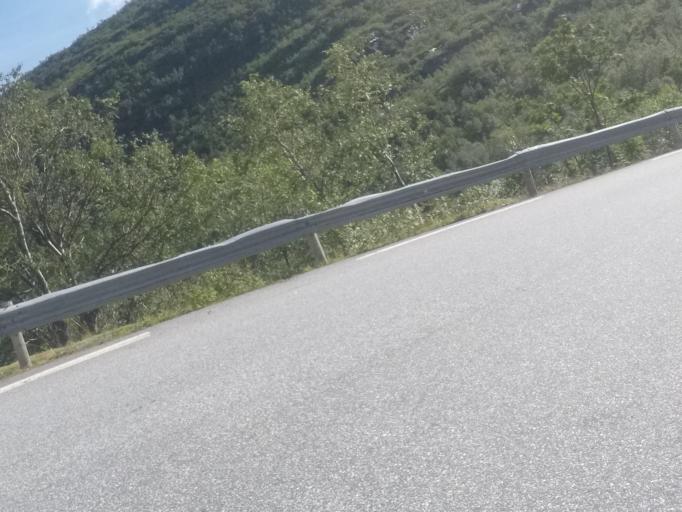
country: NO
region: Sogn og Fjordane
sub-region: Balestrand
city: Balestrand
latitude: 61.3555
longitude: 6.5312
